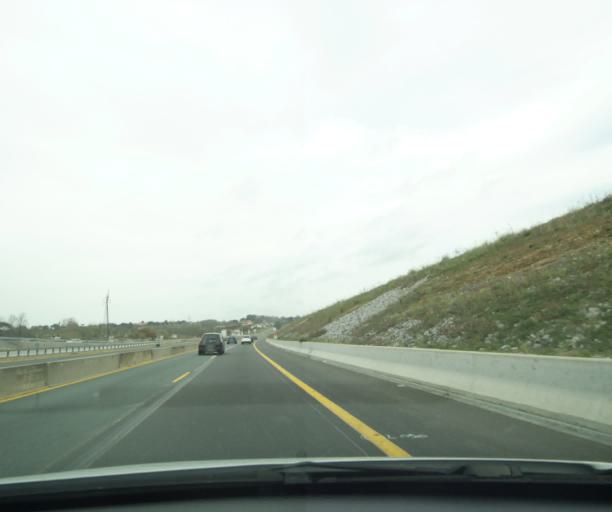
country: FR
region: Aquitaine
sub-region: Departement des Pyrenees-Atlantiques
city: Guethary
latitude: 43.4021
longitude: -1.6340
